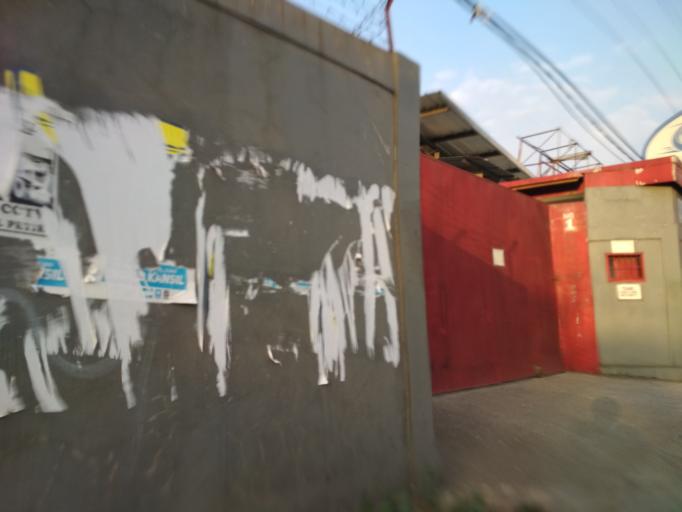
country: ID
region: West Java
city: Ciampea
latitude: -6.5588
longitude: 106.7117
